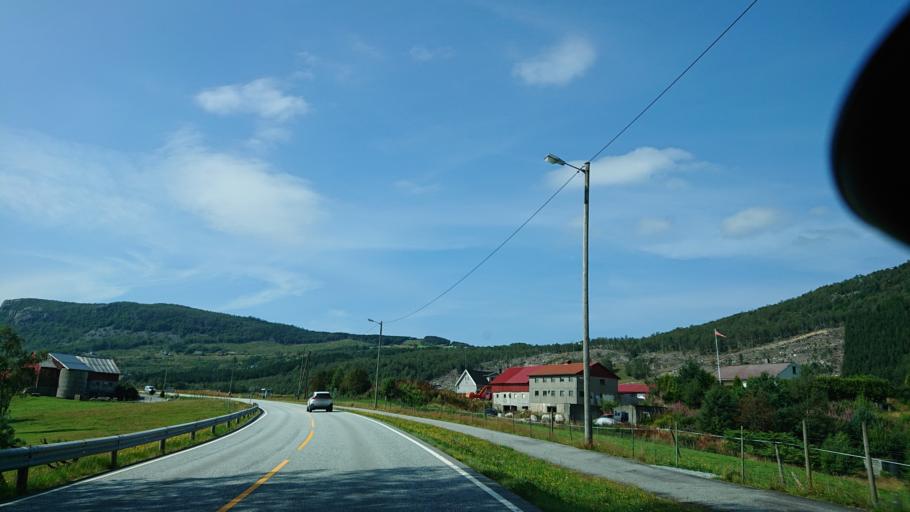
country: NO
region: Rogaland
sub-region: Strand
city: Jorpeland
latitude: 59.0743
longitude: 6.0465
